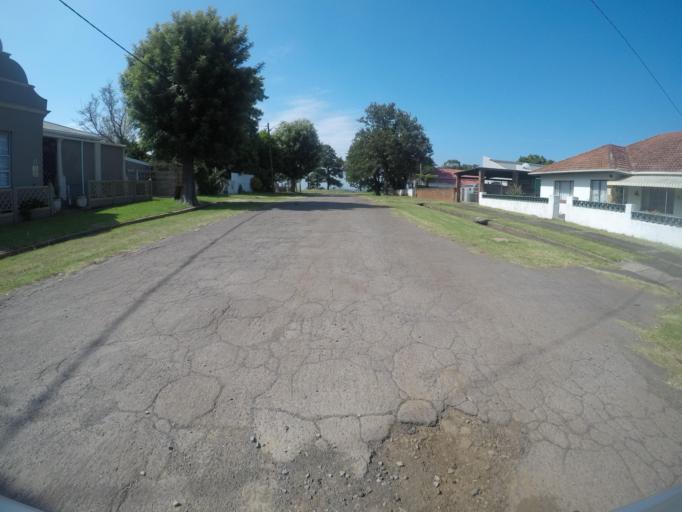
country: ZA
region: Eastern Cape
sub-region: Buffalo City Metropolitan Municipality
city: East London
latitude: -32.9692
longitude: 27.8779
